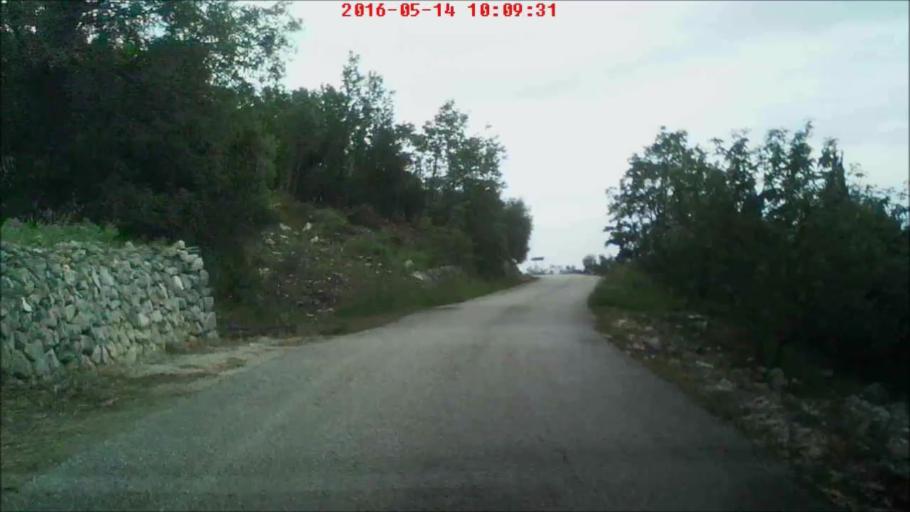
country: HR
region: Dubrovacko-Neretvanska
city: Podgora
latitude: 42.7454
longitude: 17.9373
